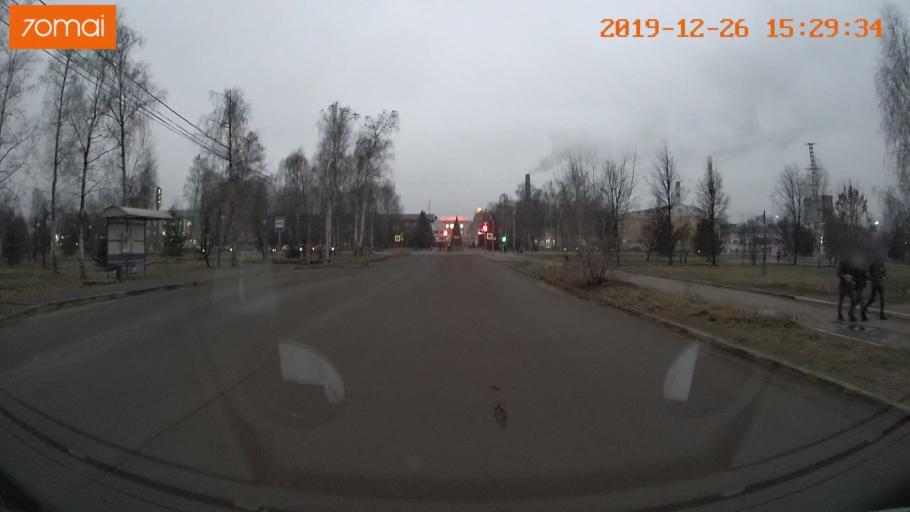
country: RU
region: Jaroslavl
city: Rybinsk
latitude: 58.0561
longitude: 38.8166
